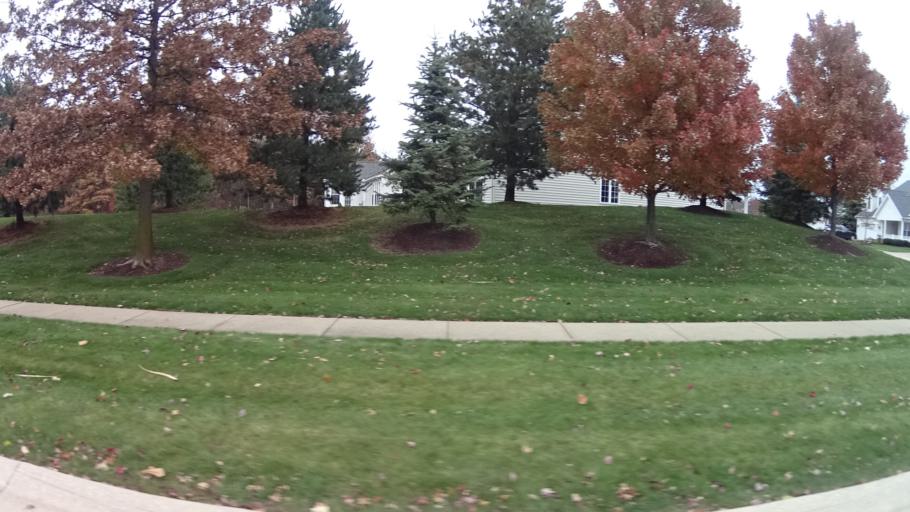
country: US
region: Ohio
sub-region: Lorain County
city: Avon Lake
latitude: 41.4902
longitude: -82.0389
